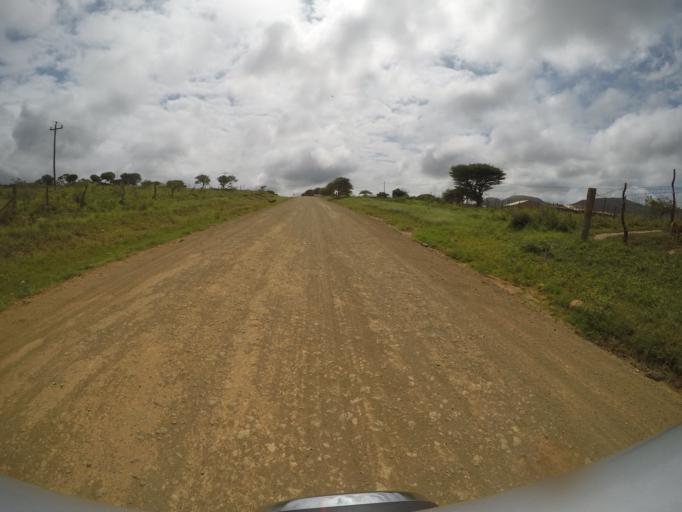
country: ZA
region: KwaZulu-Natal
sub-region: uThungulu District Municipality
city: Empangeni
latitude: -28.5810
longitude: 31.8467
